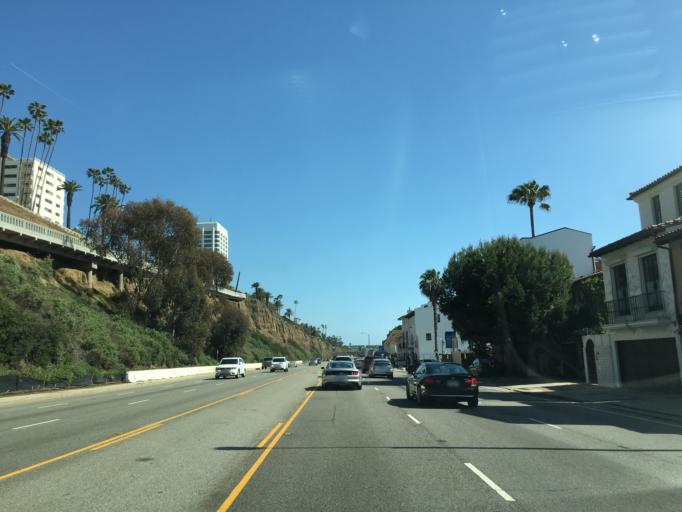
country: US
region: California
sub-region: Los Angeles County
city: Santa Monica
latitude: 34.0192
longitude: -118.5054
